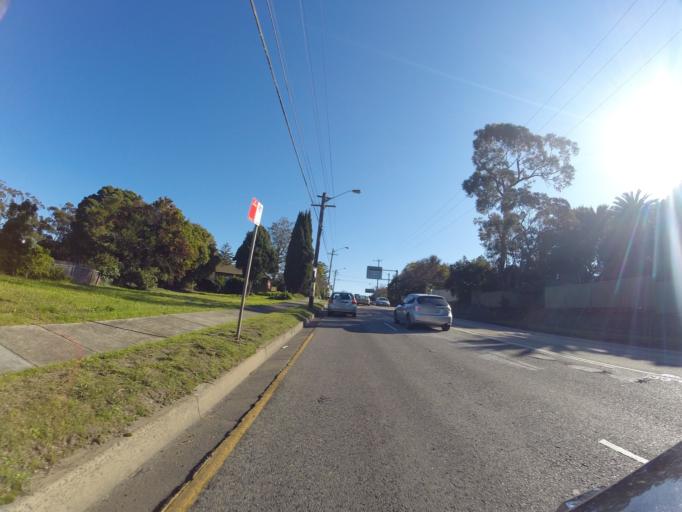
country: AU
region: New South Wales
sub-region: Kogarah
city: Hurstville Grove
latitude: -33.9705
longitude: 151.0986
